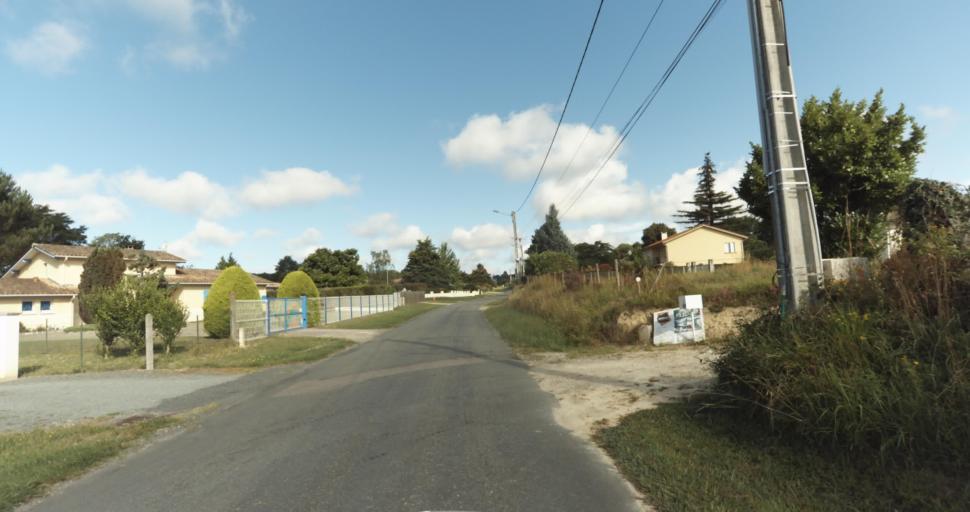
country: FR
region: Aquitaine
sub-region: Departement de la Gironde
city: Bazas
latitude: 44.4365
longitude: -0.2415
